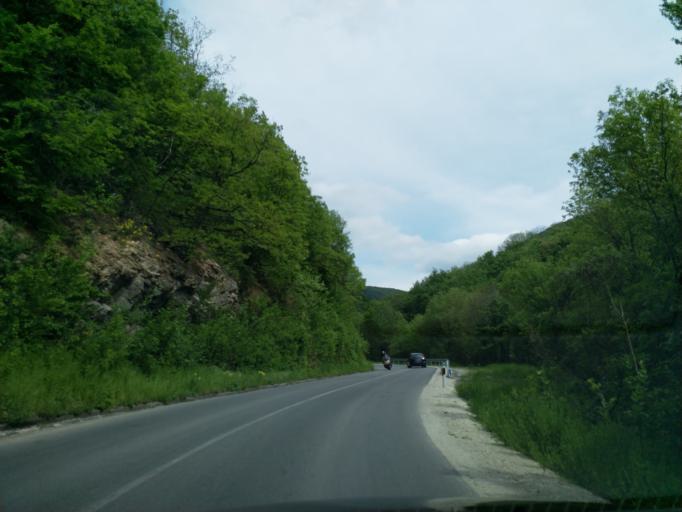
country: RS
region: Central Serbia
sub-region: Pomoravski Okrug
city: Despotovac
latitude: 43.9756
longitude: 21.5077
